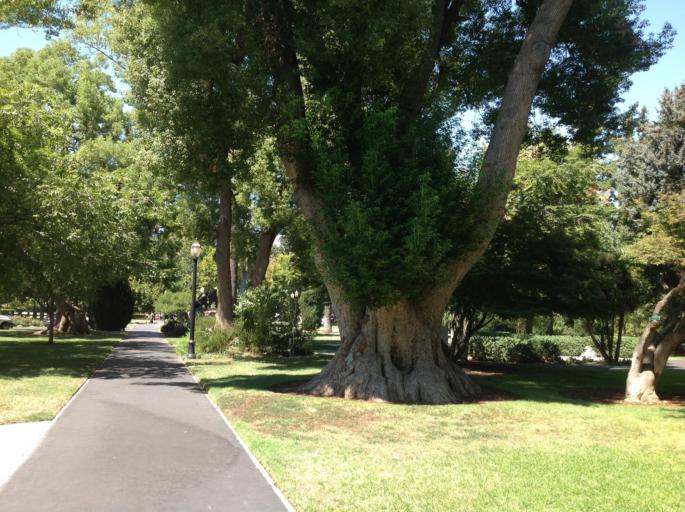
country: US
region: California
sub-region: Sacramento County
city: Sacramento
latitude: 38.5751
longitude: -121.4903
